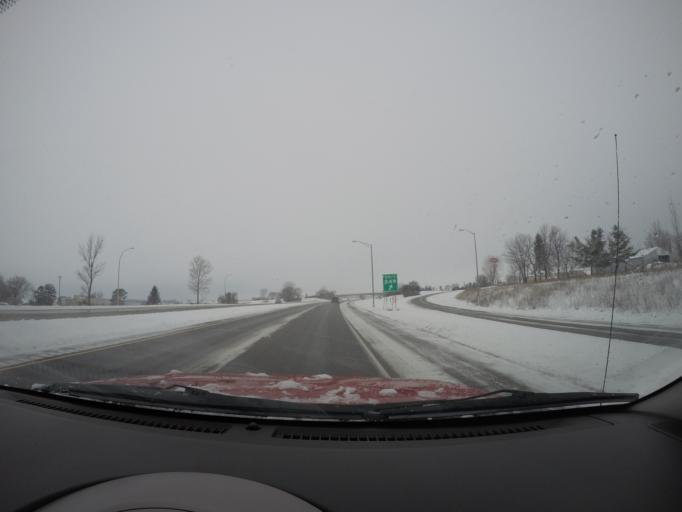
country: US
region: Minnesota
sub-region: Winona County
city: Goodview
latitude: 43.9409
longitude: -91.7411
